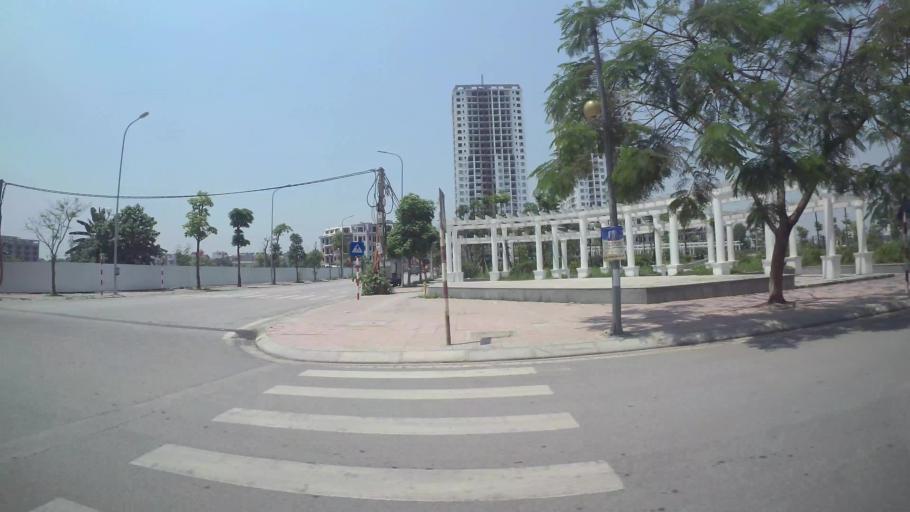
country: VN
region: Ha Noi
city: Hoan Kiem
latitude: 21.0399
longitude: 105.8784
